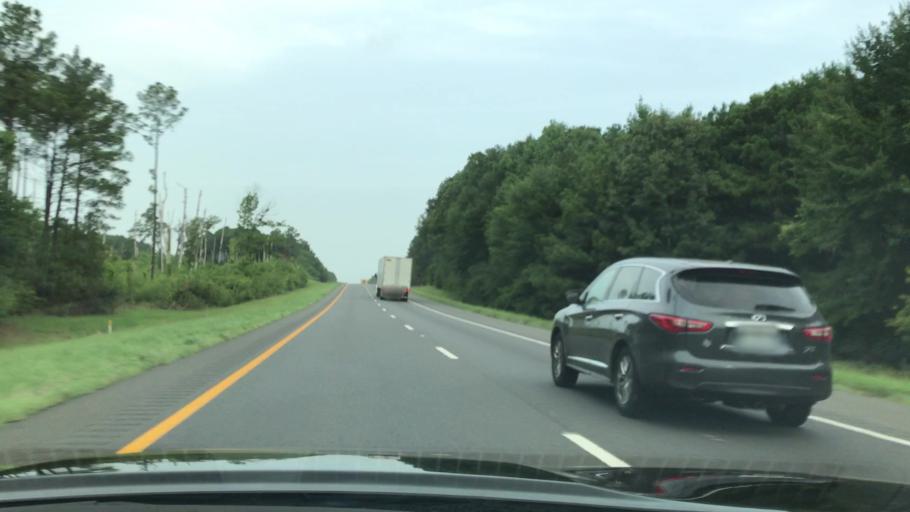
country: US
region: Texas
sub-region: Harrison County
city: Marshall
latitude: 32.4902
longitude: -94.3841
